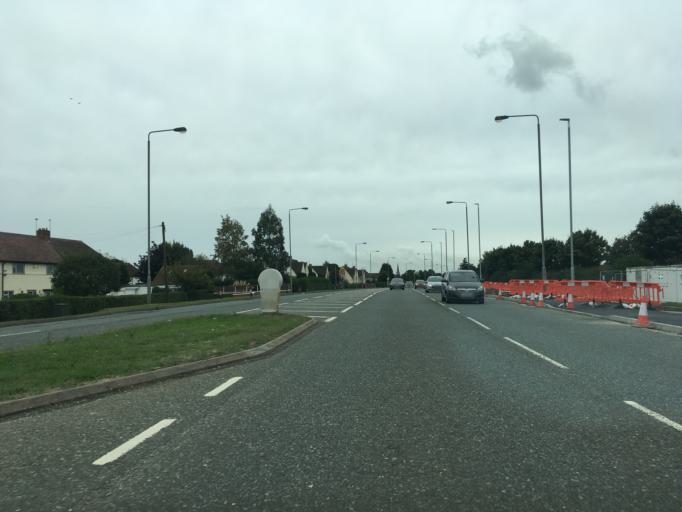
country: GB
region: England
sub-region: Nottinghamshire
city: Newark on Trent
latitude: 53.0909
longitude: -0.7908
